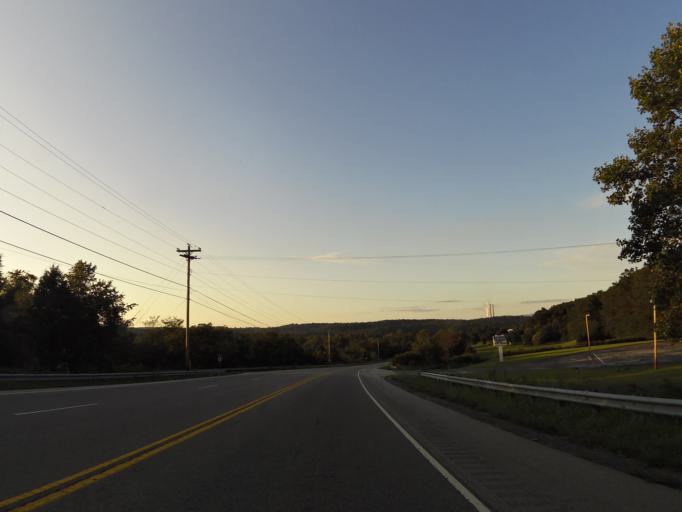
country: US
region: Tennessee
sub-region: Roane County
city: Midtown
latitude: 35.8467
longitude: -84.5429
